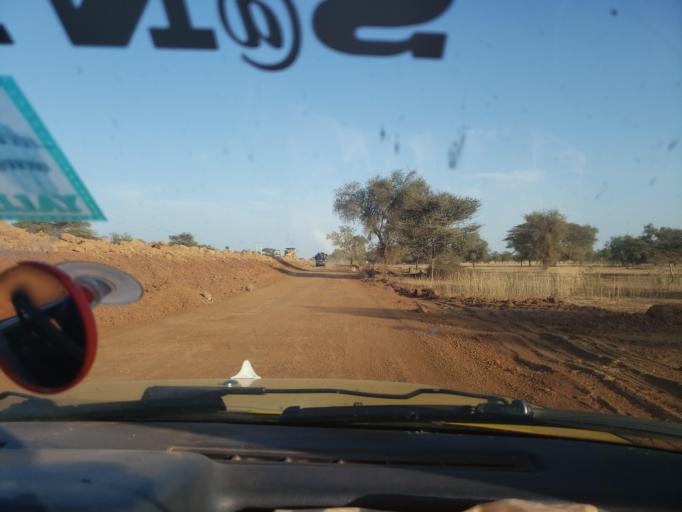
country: SN
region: Louga
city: Dara
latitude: 15.4145
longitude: -15.7079
